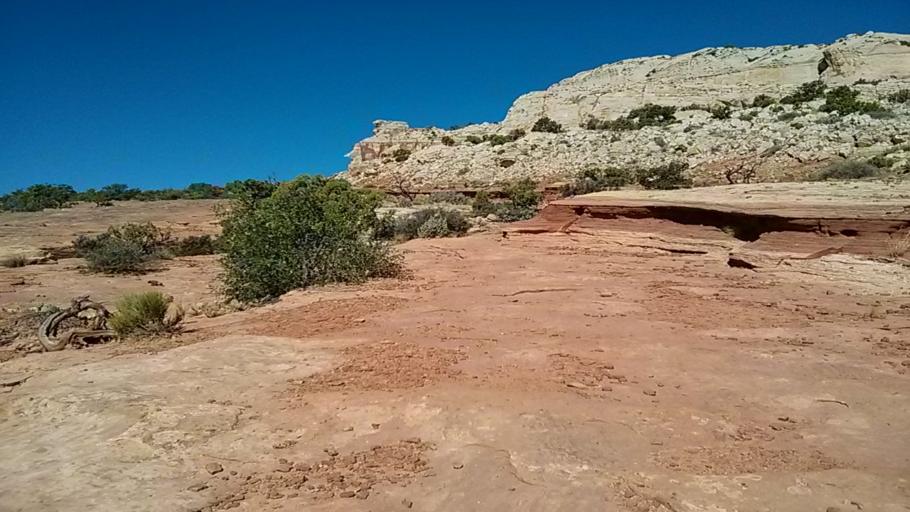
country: US
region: Utah
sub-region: Wayne County
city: Loa
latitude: 38.2922
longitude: -111.2367
